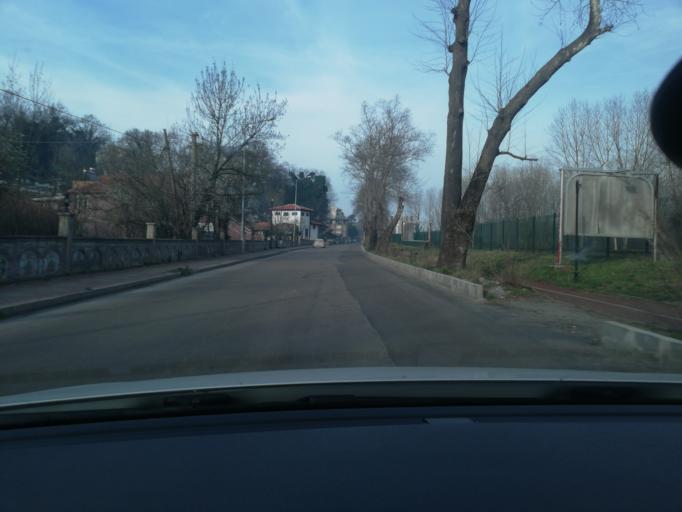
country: TR
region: Zonguldak
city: Kilimli
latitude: 41.5077
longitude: 31.8872
